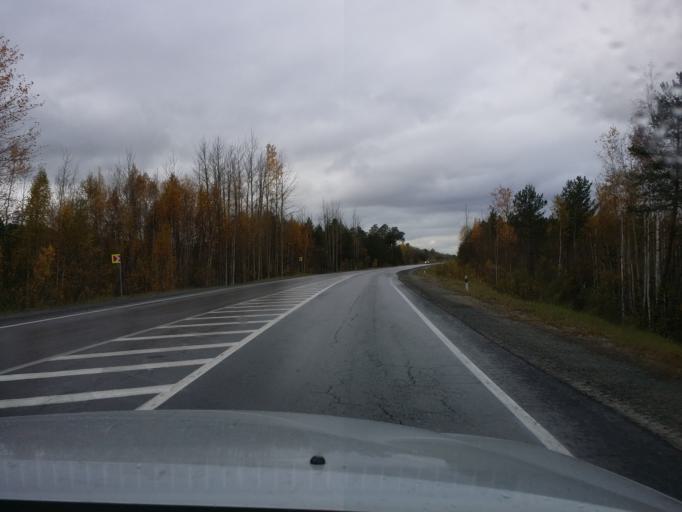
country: RU
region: Khanty-Mansiyskiy Avtonomnyy Okrug
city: Megion
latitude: 61.1015
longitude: 75.8567
